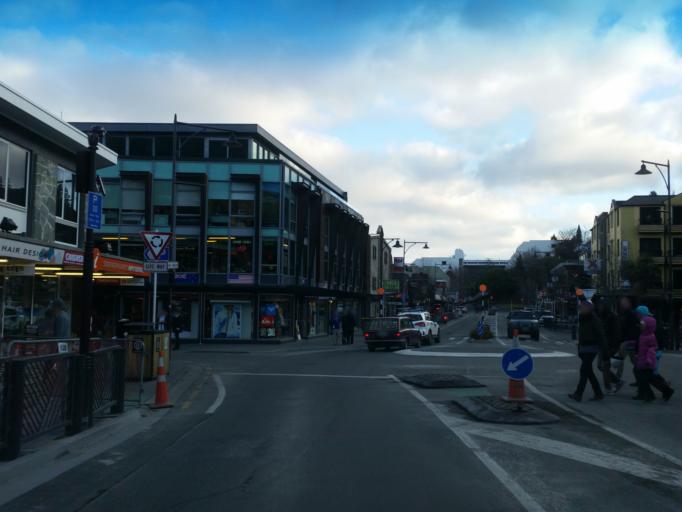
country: NZ
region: Otago
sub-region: Queenstown-Lakes District
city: Queenstown
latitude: -45.0316
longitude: 168.6594
